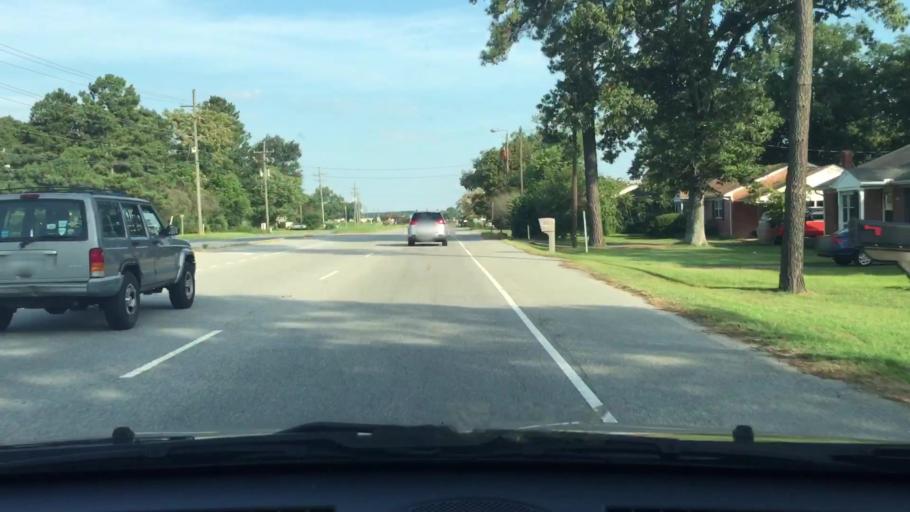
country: US
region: Virginia
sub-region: Isle of Wight County
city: Carrollton
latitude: 36.9439
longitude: -76.5910
